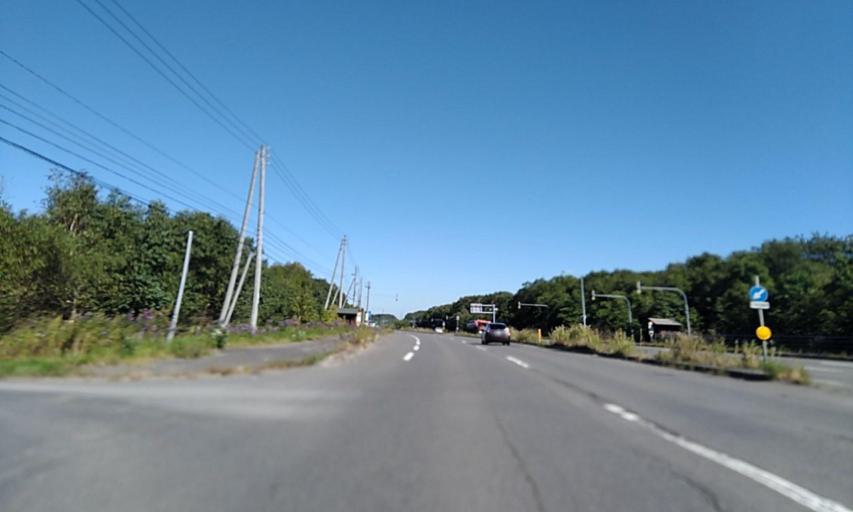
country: JP
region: Hokkaido
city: Chitose
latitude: 42.7346
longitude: 141.7092
